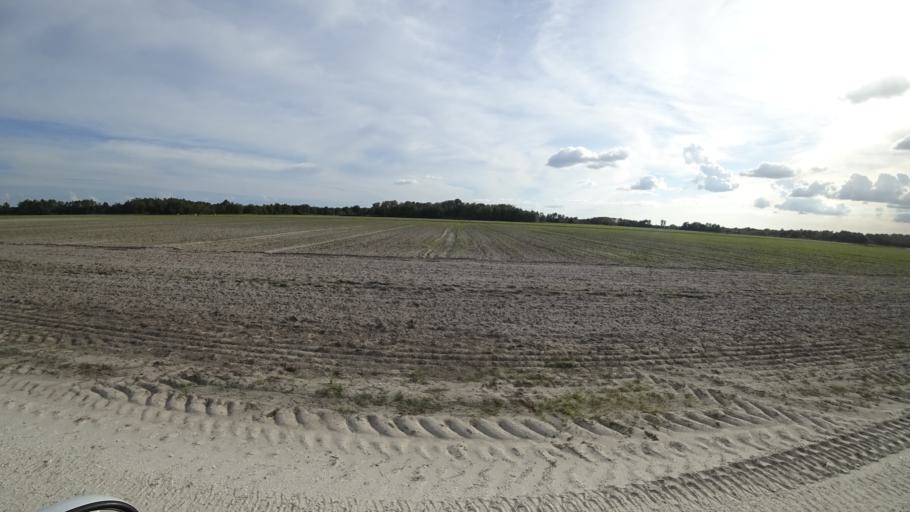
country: US
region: Florida
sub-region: Hillsborough County
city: Wimauma
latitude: 27.5665
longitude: -82.0793
